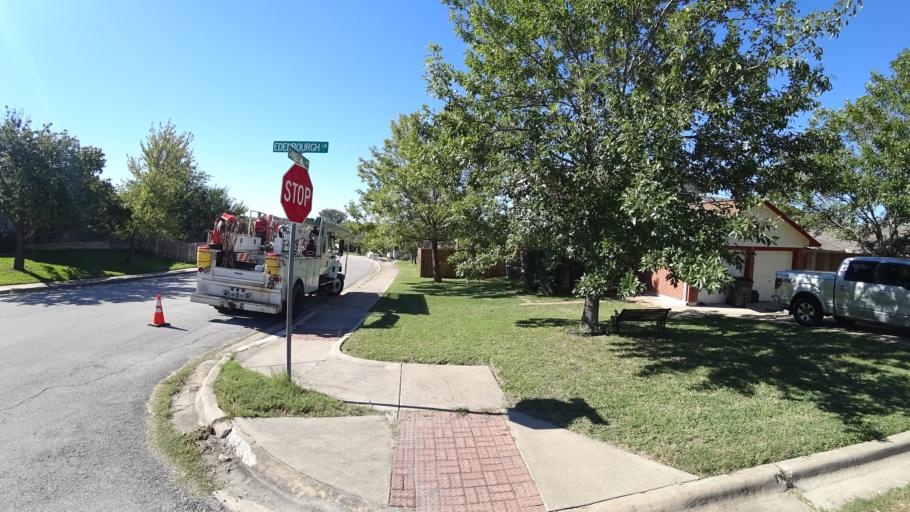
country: US
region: Texas
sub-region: Travis County
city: Manor
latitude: 30.3338
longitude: -97.6469
